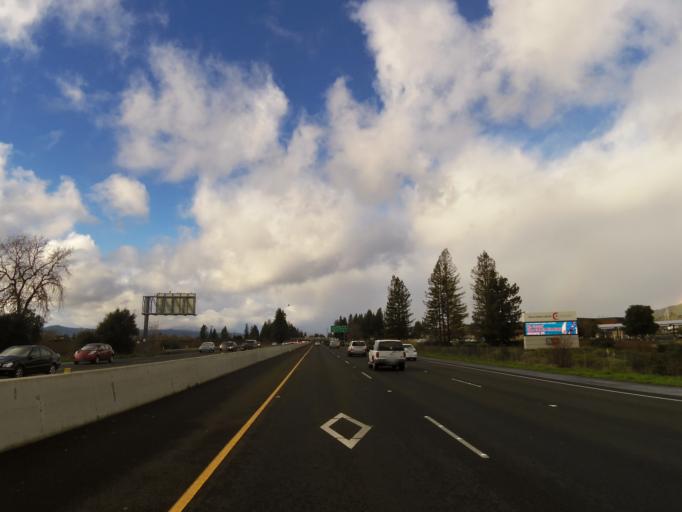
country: US
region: California
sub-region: Sonoma County
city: Larkfield-Wikiup
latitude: 38.4917
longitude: -122.7499
